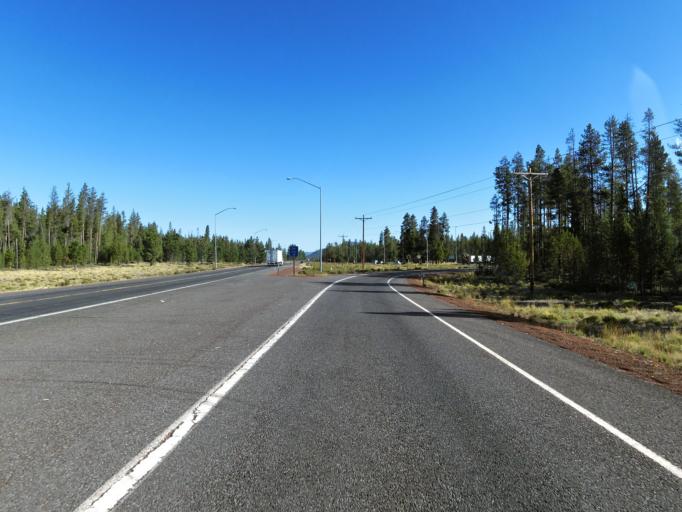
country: US
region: Oregon
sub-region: Deschutes County
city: La Pine
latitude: 43.1702
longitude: -121.7878
